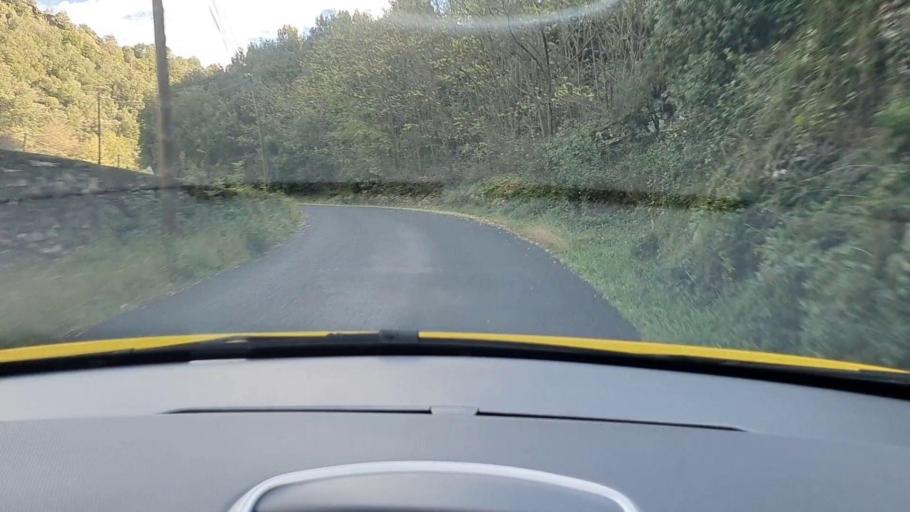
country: FR
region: Languedoc-Roussillon
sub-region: Departement du Gard
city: Sumene
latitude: 44.0114
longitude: 3.7149
